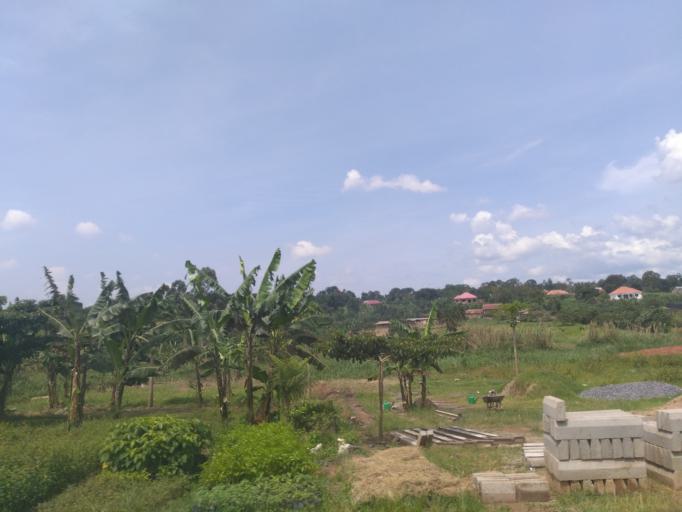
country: UG
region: Central Region
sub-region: Wakiso District
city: Bweyogerere
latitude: 0.4806
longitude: 32.6082
